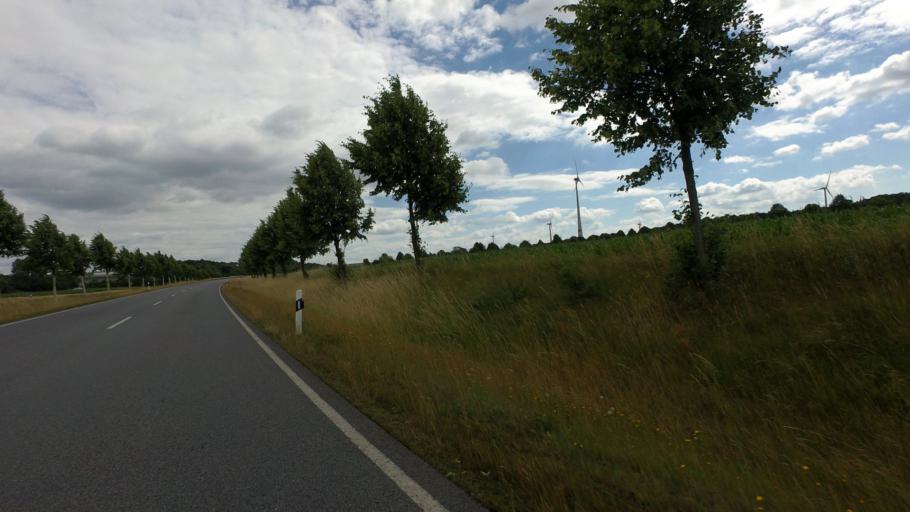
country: DE
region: Saxony
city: Nebelschutz
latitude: 51.2496
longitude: 14.1670
